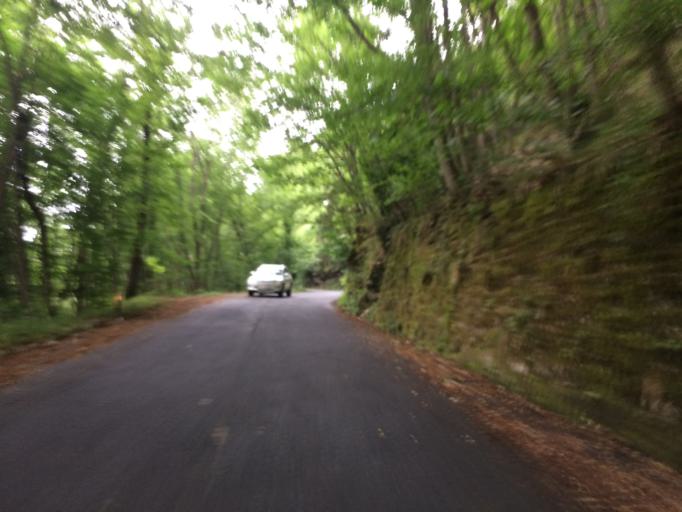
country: IT
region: Liguria
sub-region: Provincia di Imperia
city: Triora
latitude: 43.9858
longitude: 7.7587
